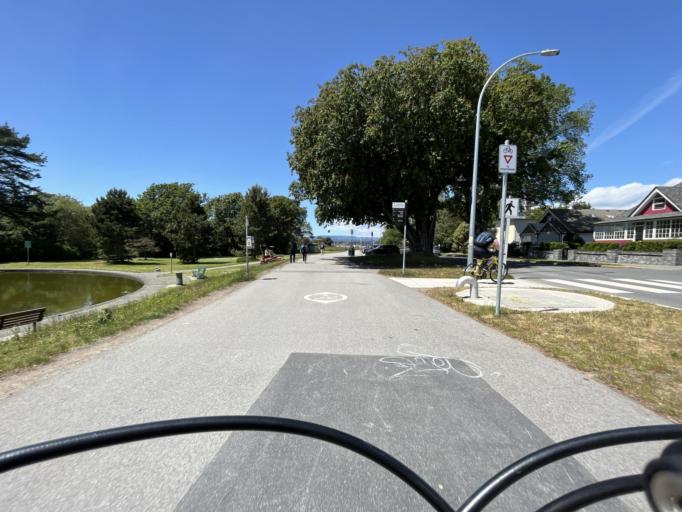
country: CA
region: British Columbia
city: Victoria
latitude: 48.4101
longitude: -123.3739
